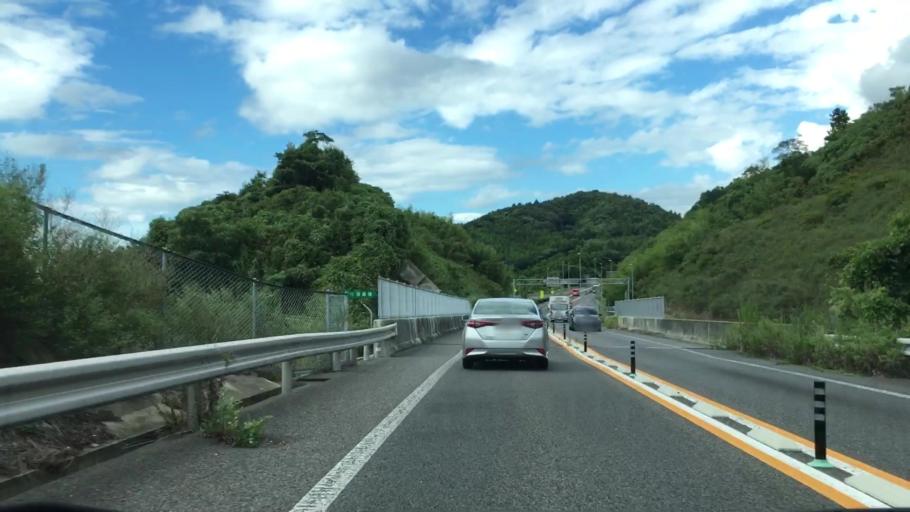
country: JP
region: Saga Prefecture
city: Karatsu
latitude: 33.4704
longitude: 130.0428
